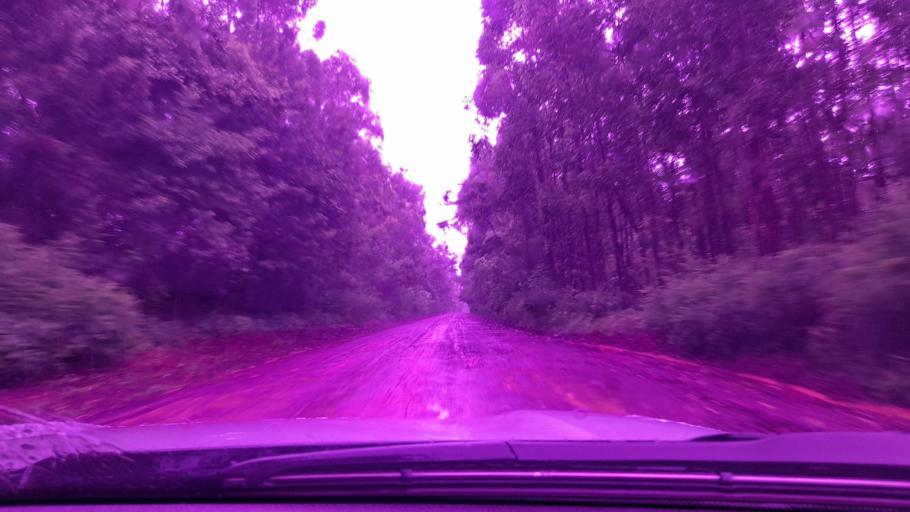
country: ET
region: Oromiya
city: Metu
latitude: 8.3267
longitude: 35.6026
